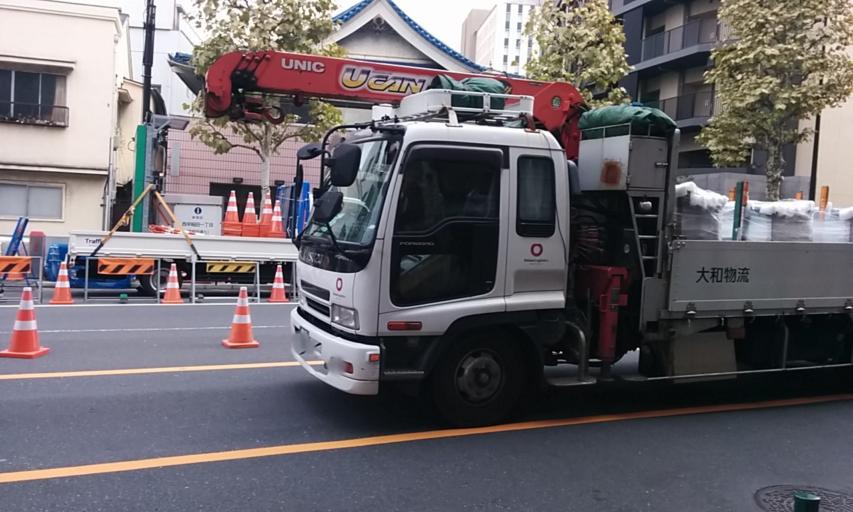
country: JP
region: Tokyo
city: Tokyo
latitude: 35.7092
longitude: 139.7166
